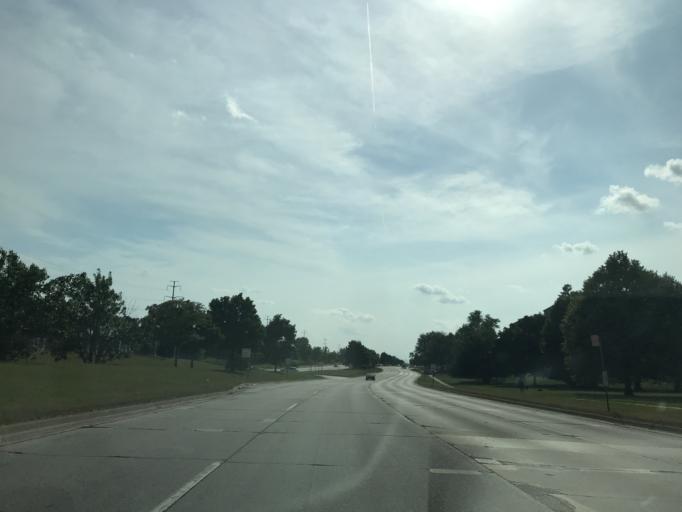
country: US
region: Michigan
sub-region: Wayne County
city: Inkster
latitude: 42.2871
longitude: -83.3393
